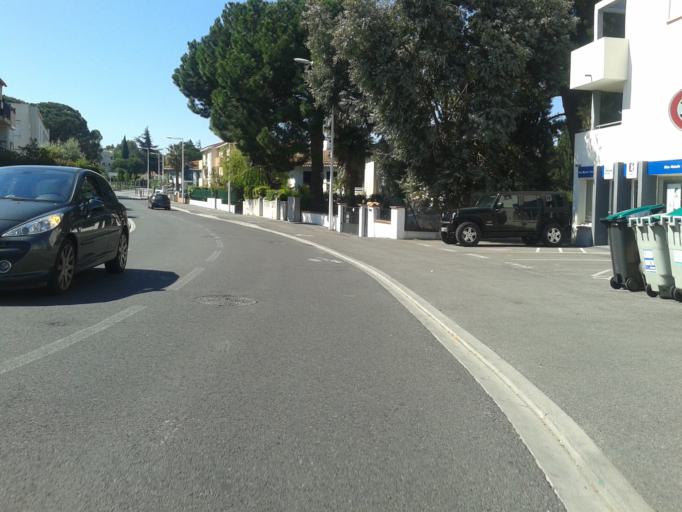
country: FR
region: Languedoc-Roussillon
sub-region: Departement des Pyrenees-Orientales
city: Perpignan
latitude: 42.6863
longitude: 2.8993
